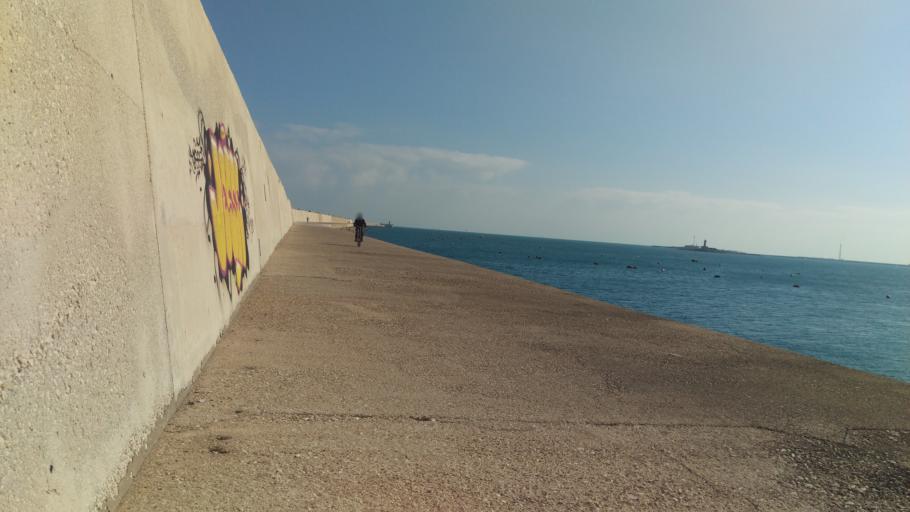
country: IT
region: Apulia
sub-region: Provincia di Brindisi
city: Materdomini
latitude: 40.6630
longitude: 17.9758
